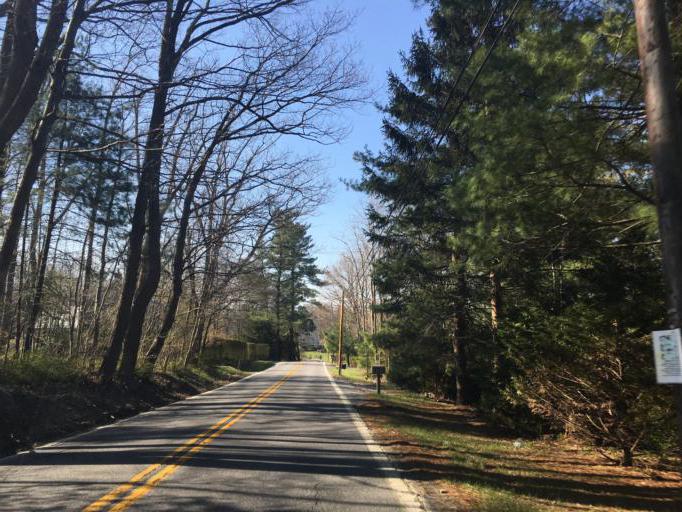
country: US
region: Maryland
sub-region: Washington County
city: Cavetown
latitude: 39.5936
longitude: -77.5588
